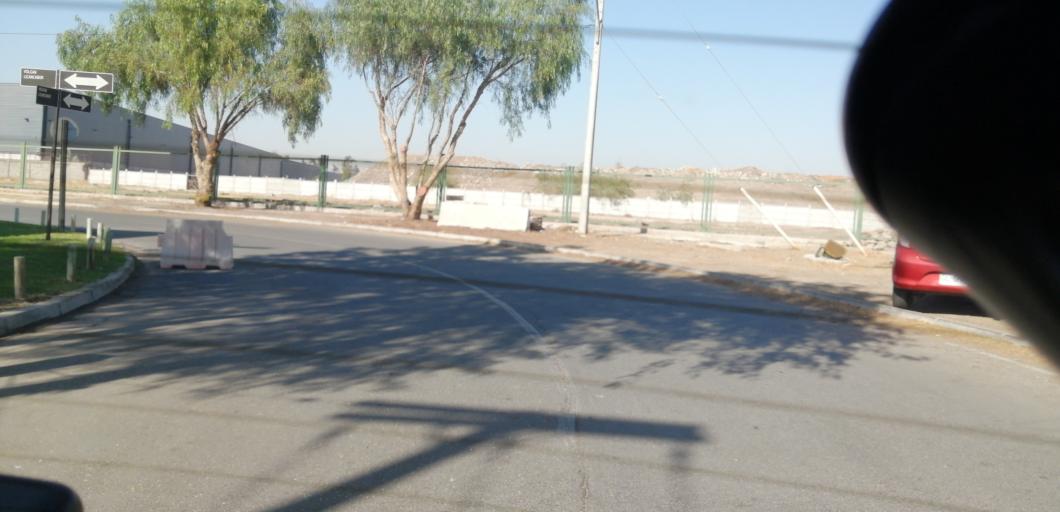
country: CL
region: Santiago Metropolitan
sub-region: Provincia de Santiago
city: Lo Prado
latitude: -33.3834
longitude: -70.7796
